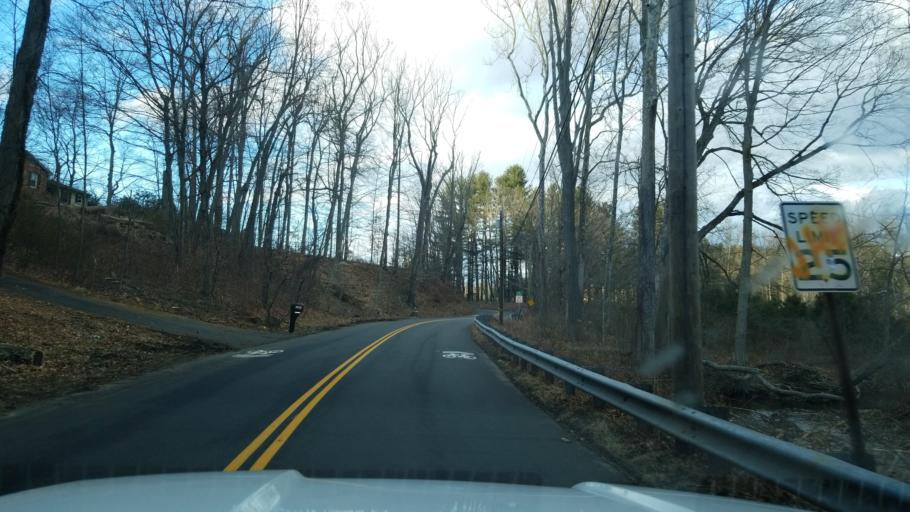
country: US
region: Connecticut
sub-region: Middlesex County
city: Durham
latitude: 41.5051
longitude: -72.6326
